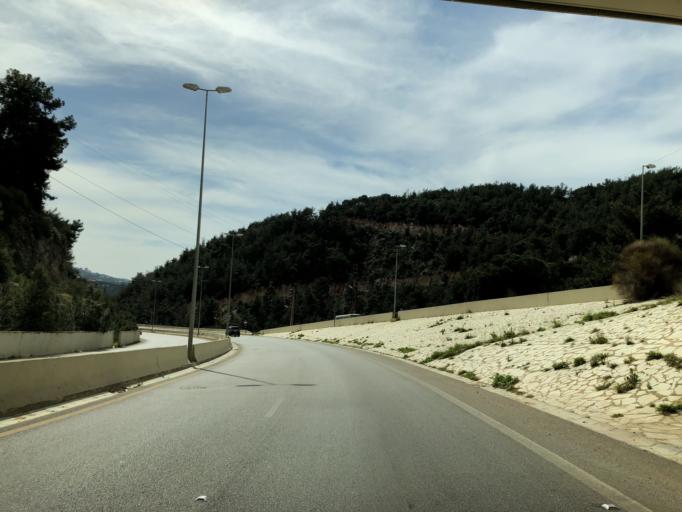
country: LB
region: Mont-Liban
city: Jdaidet el Matn
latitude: 33.8983
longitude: 35.6342
